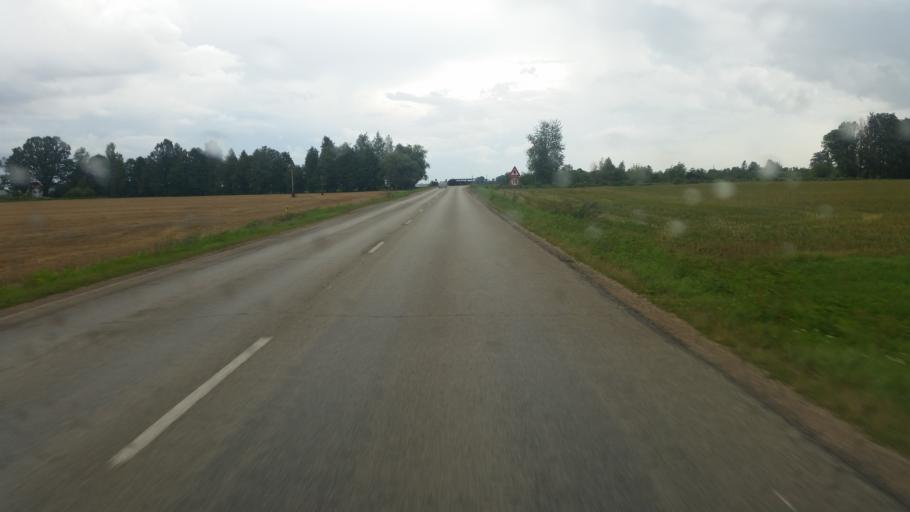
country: LV
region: Bauskas Rajons
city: Bauska
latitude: 56.4247
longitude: 24.2245
